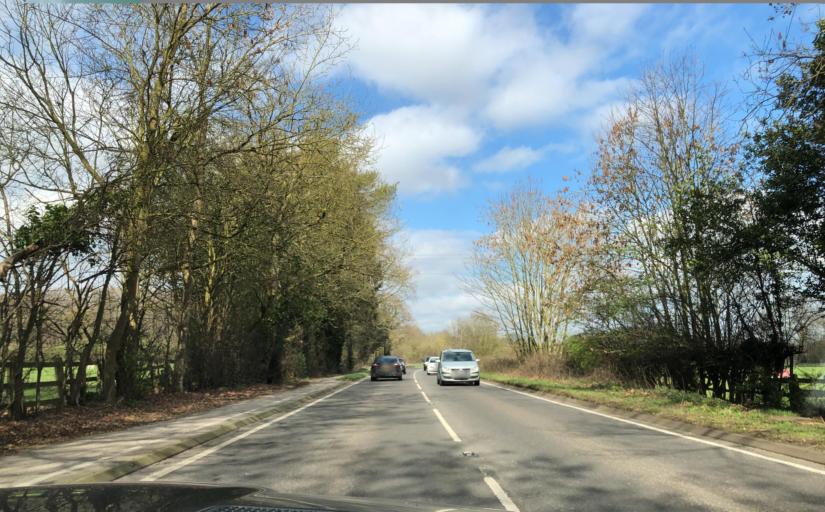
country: GB
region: England
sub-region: Warwickshire
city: Warwick
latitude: 52.3015
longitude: -1.5753
